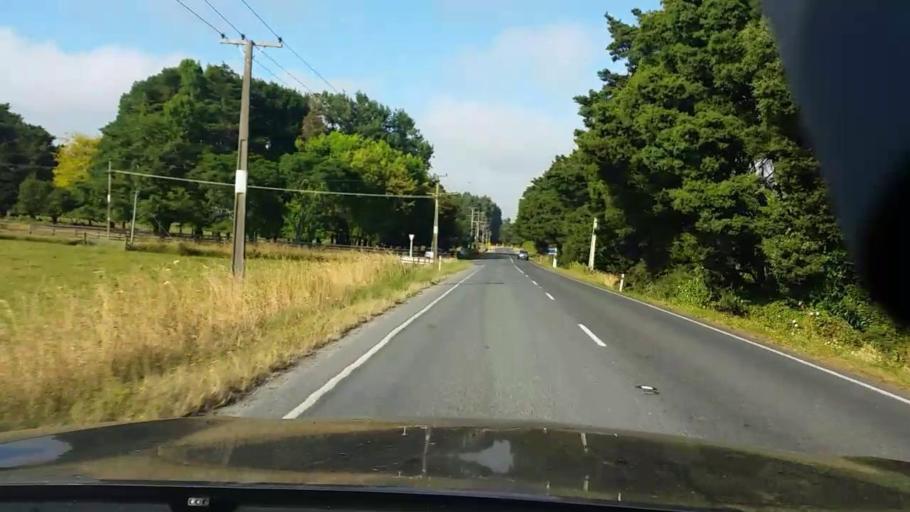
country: NZ
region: Waikato
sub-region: Hamilton City
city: Hamilton
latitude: -37.5949
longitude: 175.3611
